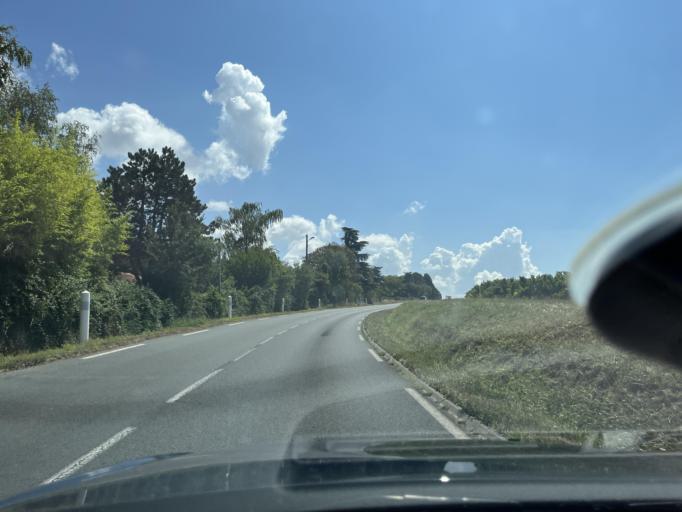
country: FR
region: Aquitaine
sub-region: Departement de la Gironde
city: Cantenac
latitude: 45.0705
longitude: -0.6247
